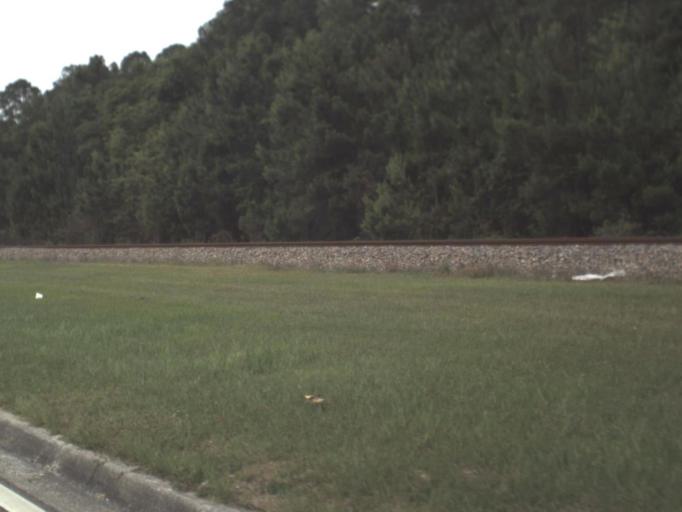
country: US
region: Florida
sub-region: Clay County
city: Orange Park
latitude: 30.2434
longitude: -81.6969
